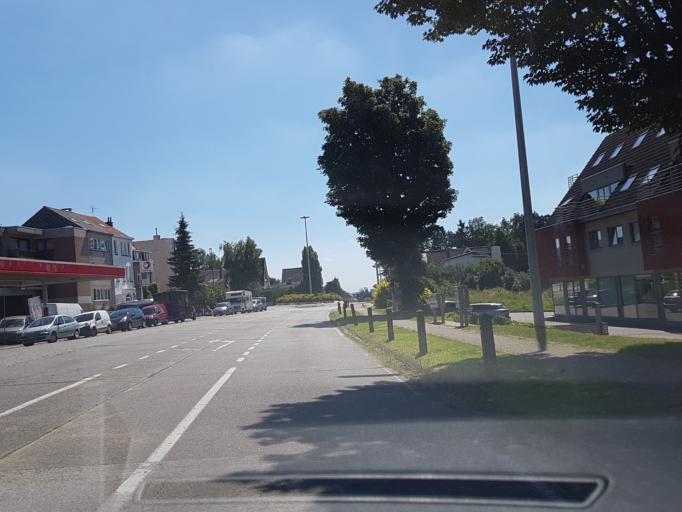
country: BE
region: Flanders
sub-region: Provincie Vlaams-Brabant
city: Dilbeek
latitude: 50.8891
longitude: 4.2661
